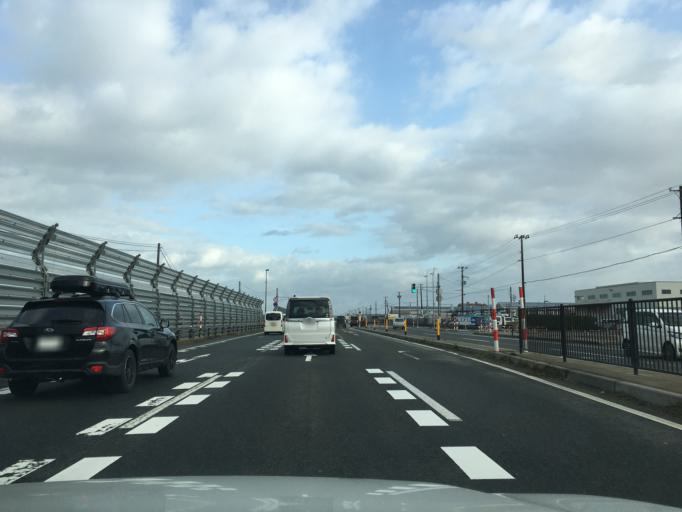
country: JP
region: Yamagata
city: Sakata
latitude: 38.8604
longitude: 139.8448
